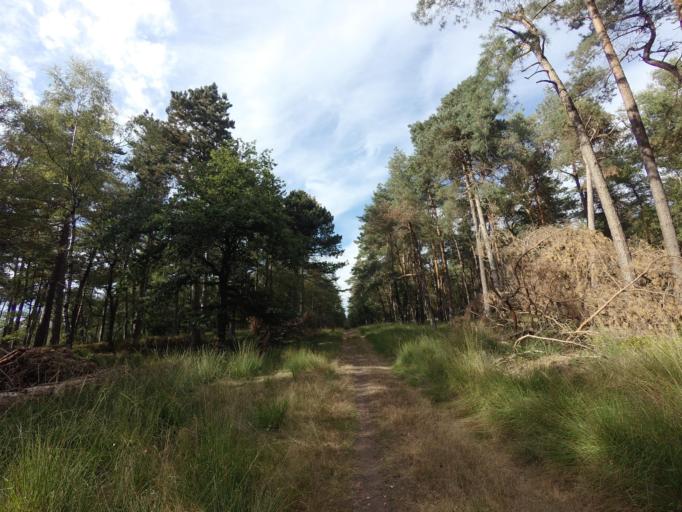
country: NL
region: Gelderland
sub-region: Gemeente Brummen
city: Eerbeek
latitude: 52.0643
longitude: 6.0321
